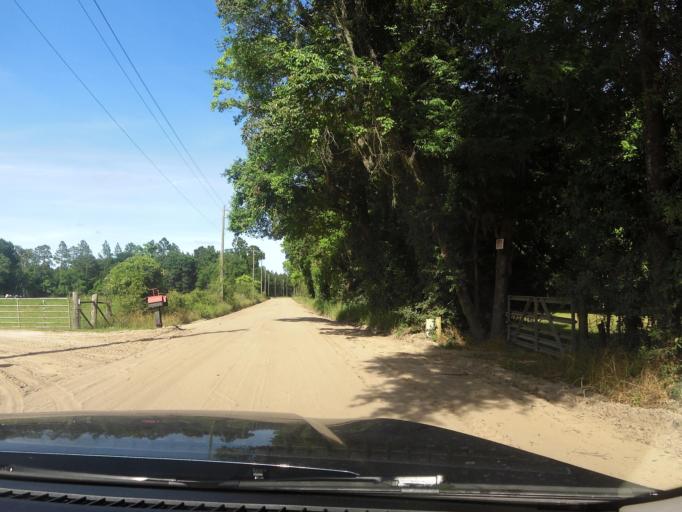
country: US
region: Florida
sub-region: Nassau County
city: Callahan
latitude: 30.5667
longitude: -81.7854
